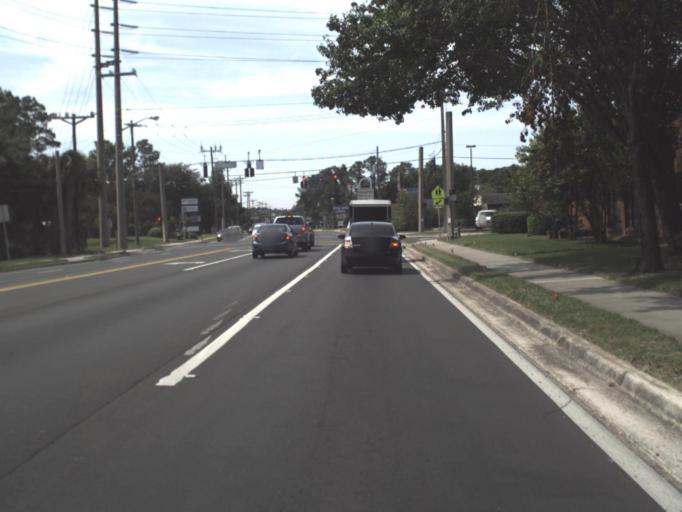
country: US
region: Florida
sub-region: Duval County
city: Jacksonville
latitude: 30.2847
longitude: -81.6028
